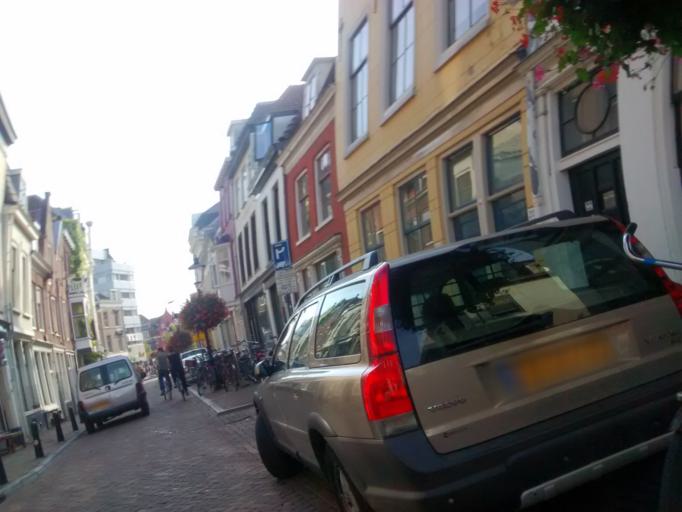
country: NL
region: Utrecht
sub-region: Gemeente Utrecht
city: Utrecht
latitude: 52.0946
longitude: 5.1186
